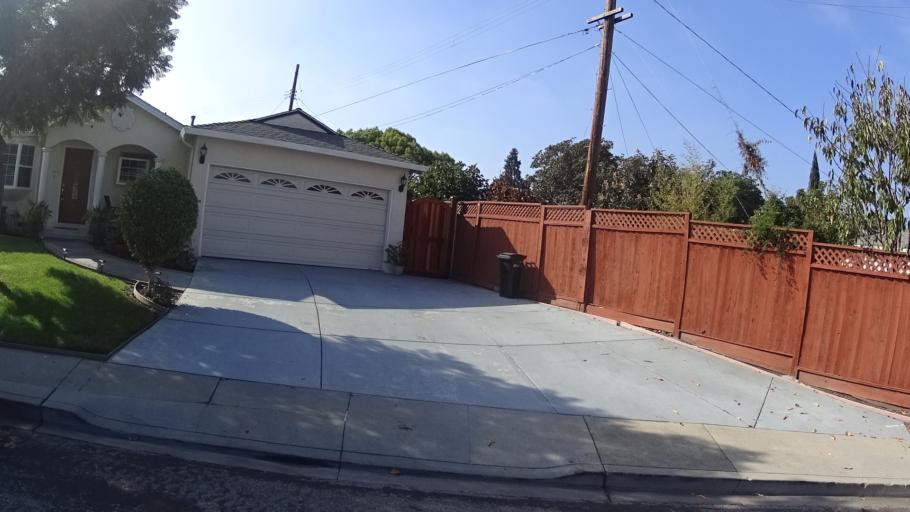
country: US
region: California
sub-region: Santa Clara County
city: Santa Clara
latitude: 37.3550
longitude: -121.9893
